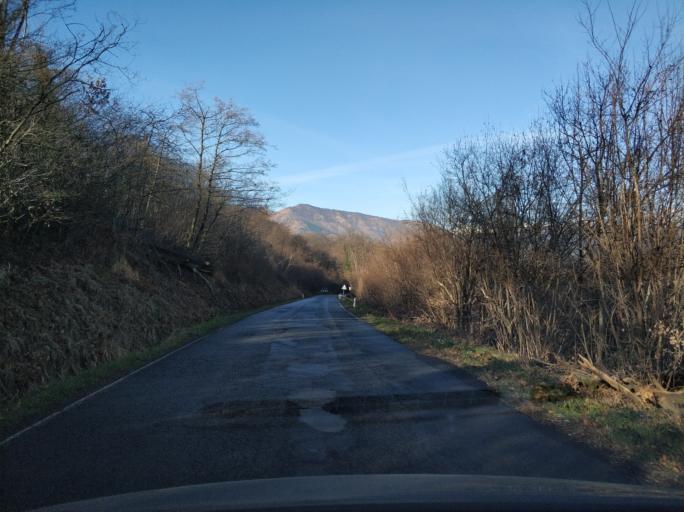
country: IT
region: Piedmont
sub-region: Provincia di Torino
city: Robassomero
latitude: 45.2117
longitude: 7.5503
